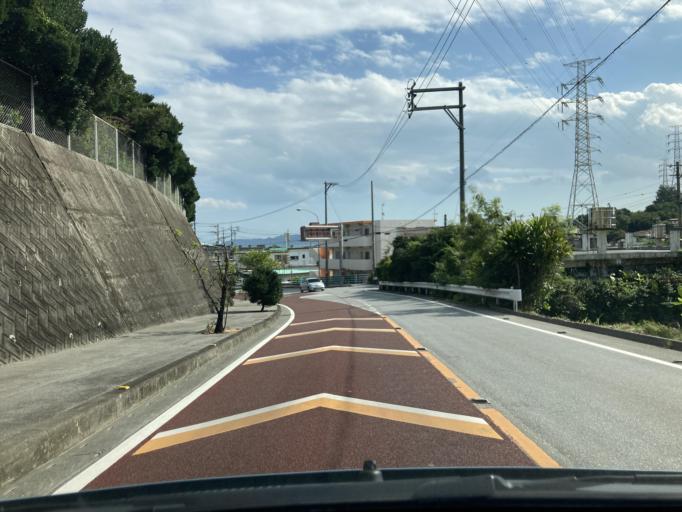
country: JP
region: Okinawa
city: Ginowan
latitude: 26.2563
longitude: 127.7840
